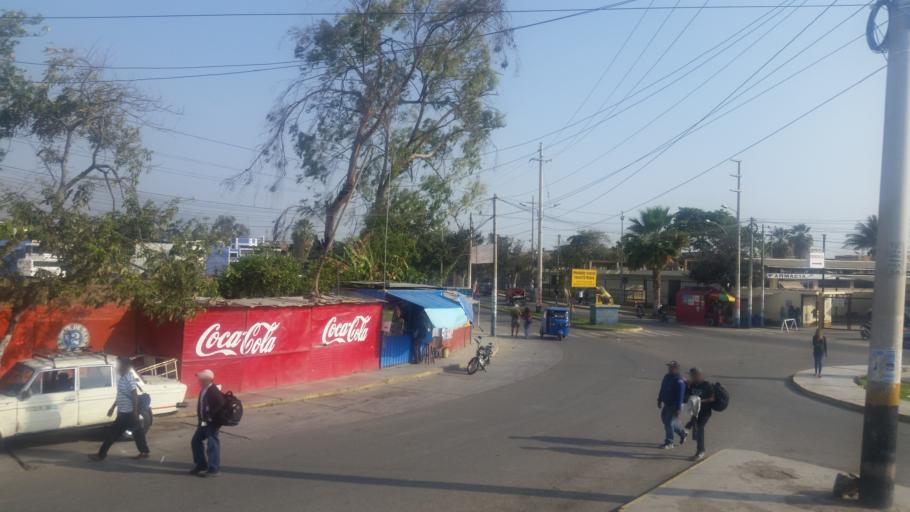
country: PE
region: La Libertad
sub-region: Chepen
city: Chepen
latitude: -7.2209
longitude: -79.4360
